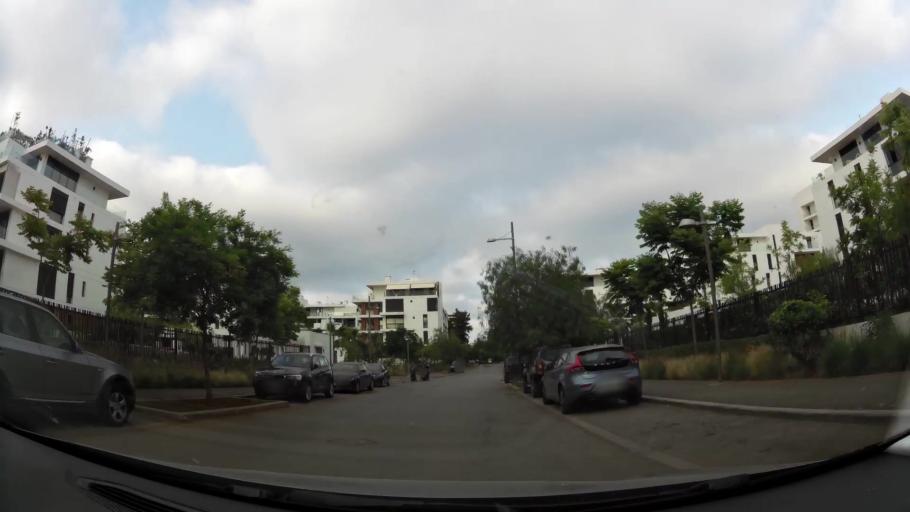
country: MA
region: Rabat-Sale-Zemmour-Zaer
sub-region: Rabat
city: Rabat
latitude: 33.9508
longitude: -6.8348
